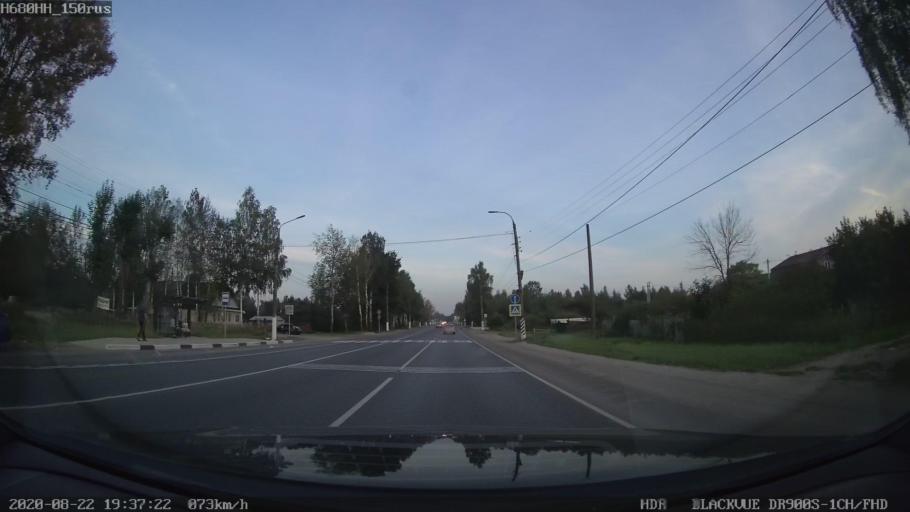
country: RU
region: Tverskaya
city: Tver
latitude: 56.8190
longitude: 35.9819
